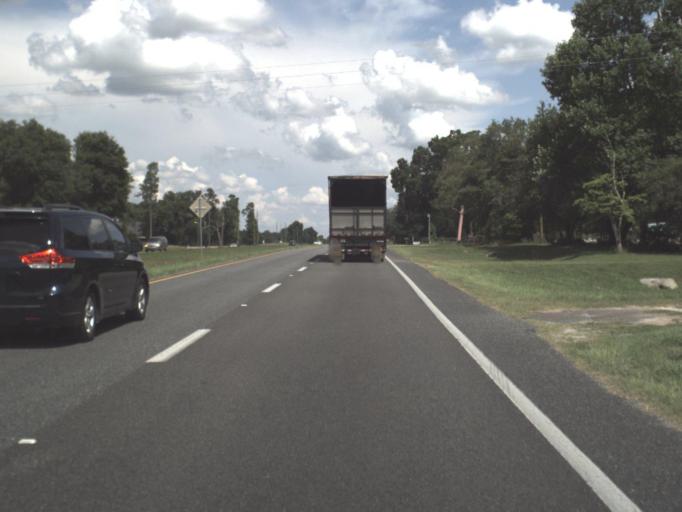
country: US
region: Florida
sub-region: Alachua County
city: High Springs
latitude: 29.8167
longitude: -82.5735
